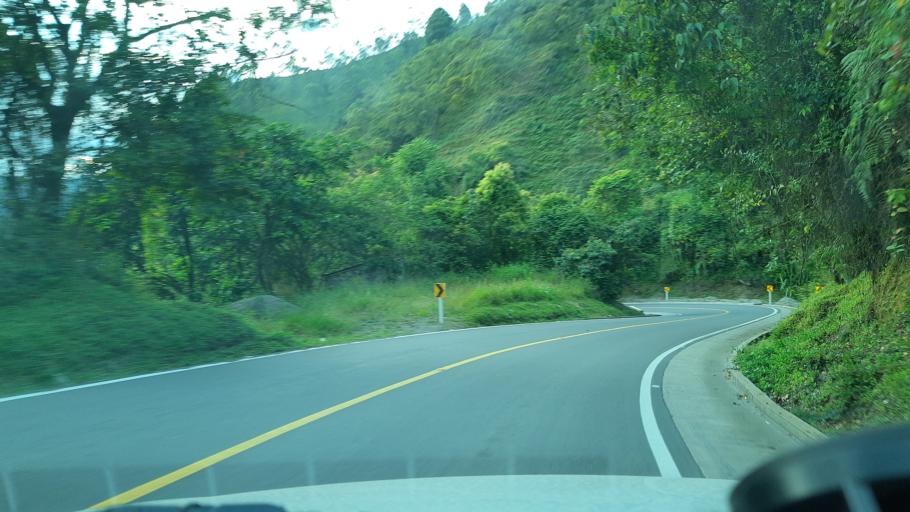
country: CO
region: Boyaca
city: Chivor
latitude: 4.9781
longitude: -73.3347
